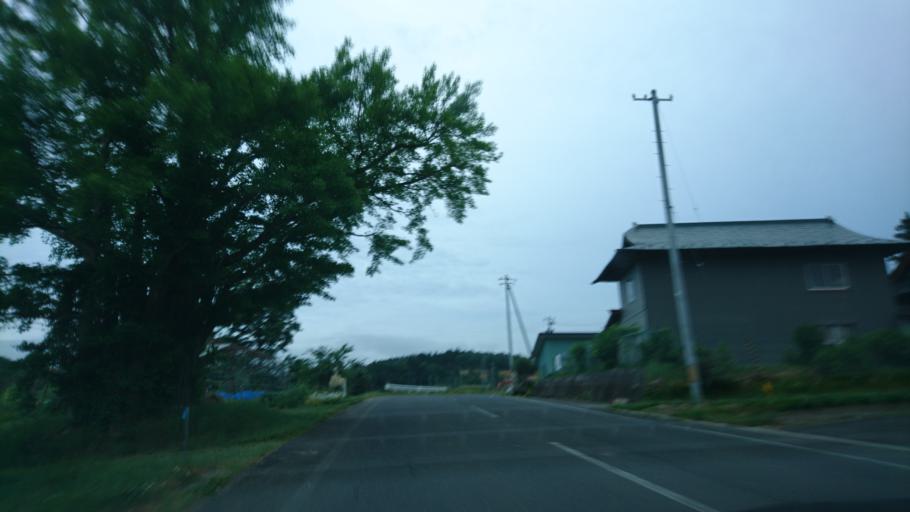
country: JP
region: Iwate
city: Ichinoseki
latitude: 38.9203
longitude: 141.1739
